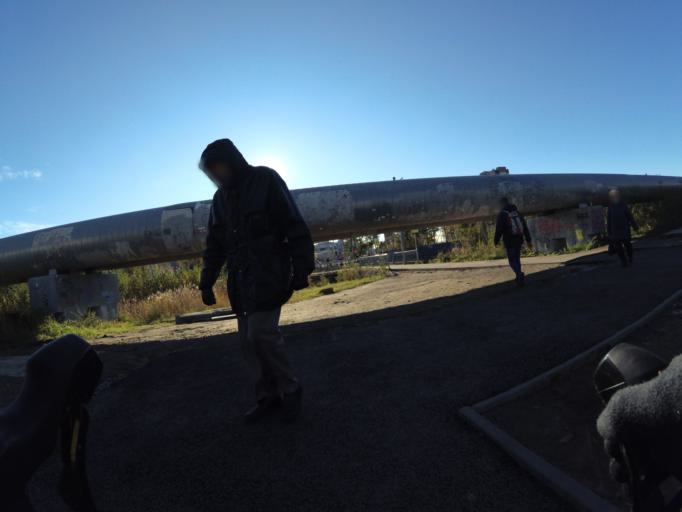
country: RU
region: Leningrad
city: Untolovo
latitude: 59.9941
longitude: 30.2043
